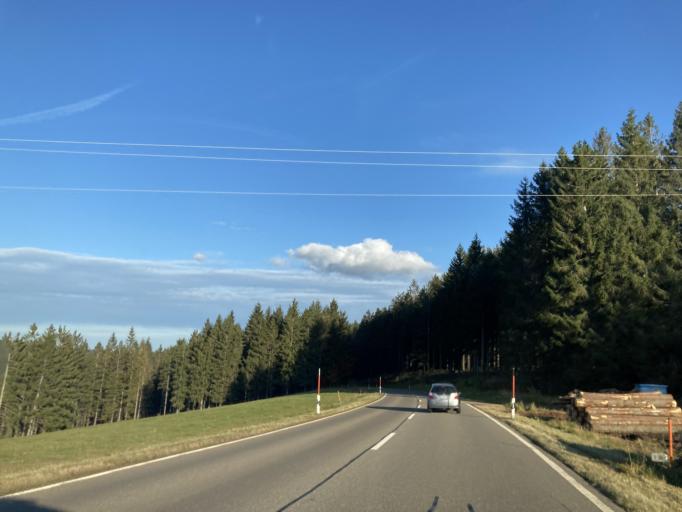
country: DE
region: Baden-Wuerttemberg
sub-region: Freiburg Region
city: Gutenbach
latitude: 47.9936
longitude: 8.1800
